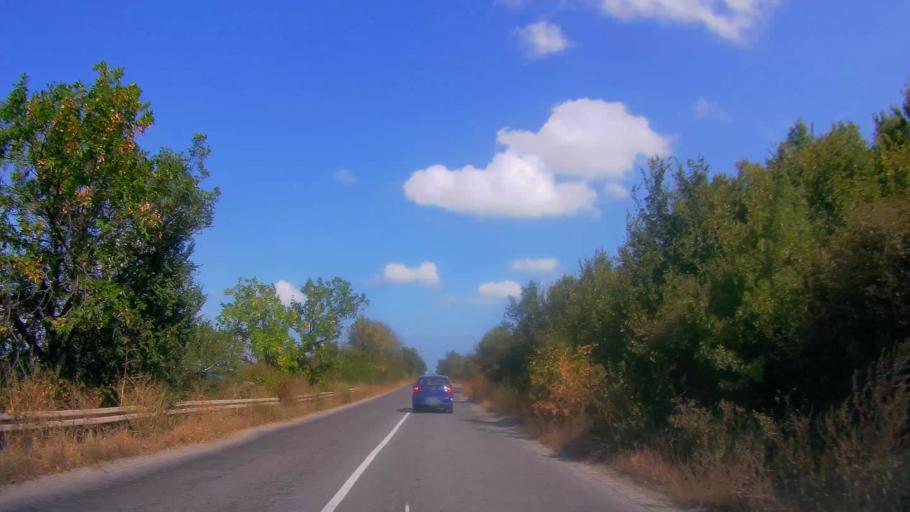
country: BG
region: Burgas
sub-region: Obshtina Burgas
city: Burgas
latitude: 42.4773
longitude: 27.4084
